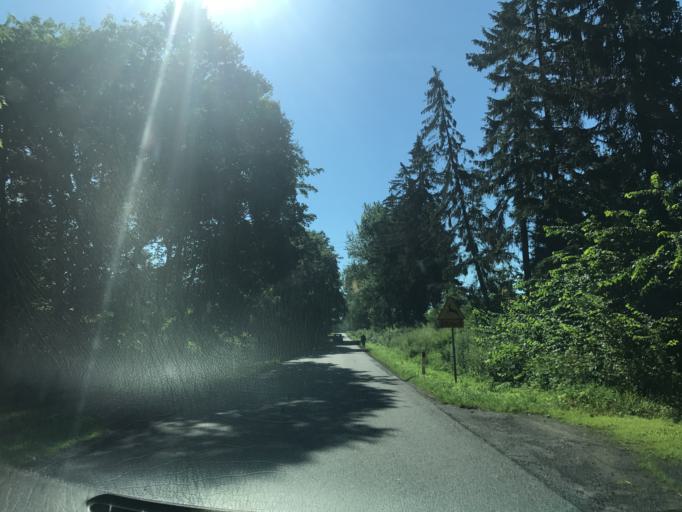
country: PL
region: Pomeranian Voivodeship
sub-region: Powiat slupski
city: Potegowo
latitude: 54.4125
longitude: 17.4164
